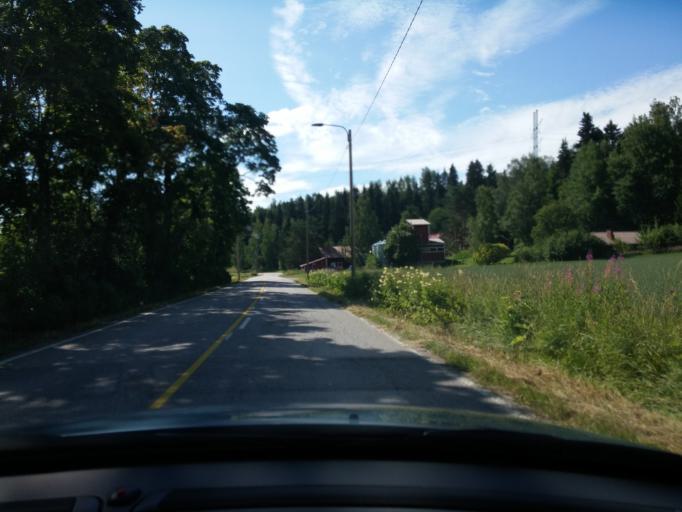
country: FI
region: Uusimaa
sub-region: Porvoo
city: Porvoo
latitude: 60.4318
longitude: 25.5935
